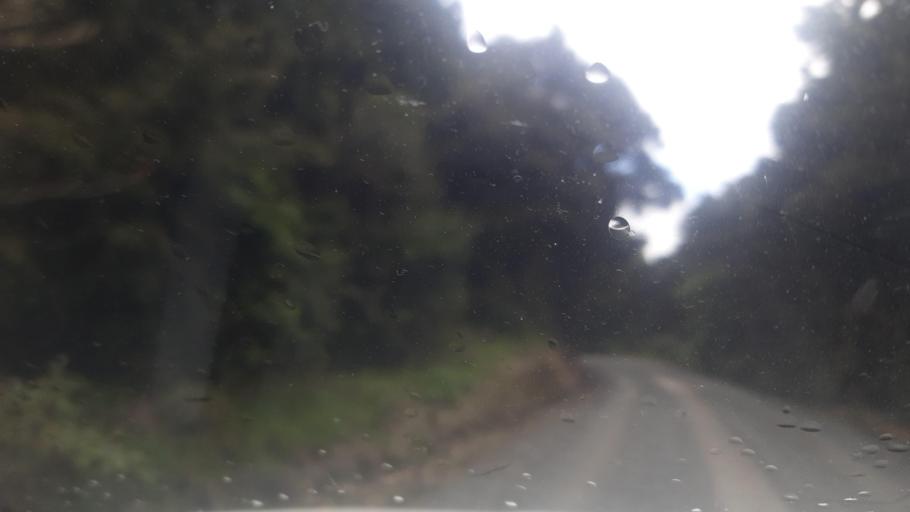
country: NZ
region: Northland
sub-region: Far North District
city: Taipa
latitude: -35.0464
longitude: 173.3927
